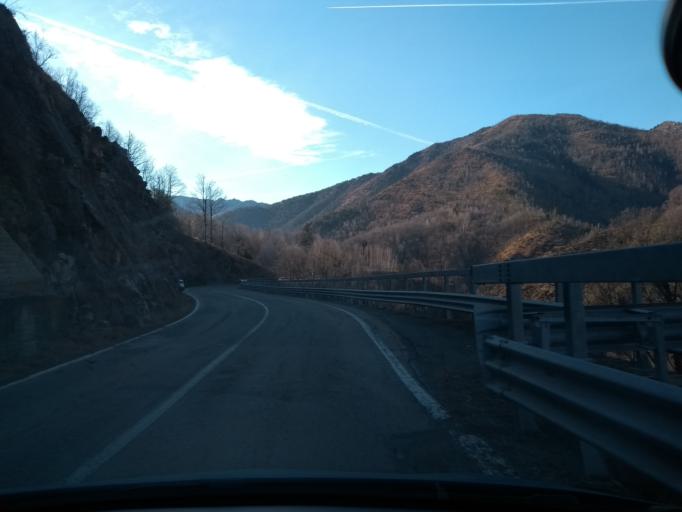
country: IT
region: Piedmont
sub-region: Provincia di Torino
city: La Villa
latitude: 45.2592
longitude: 7.4391
